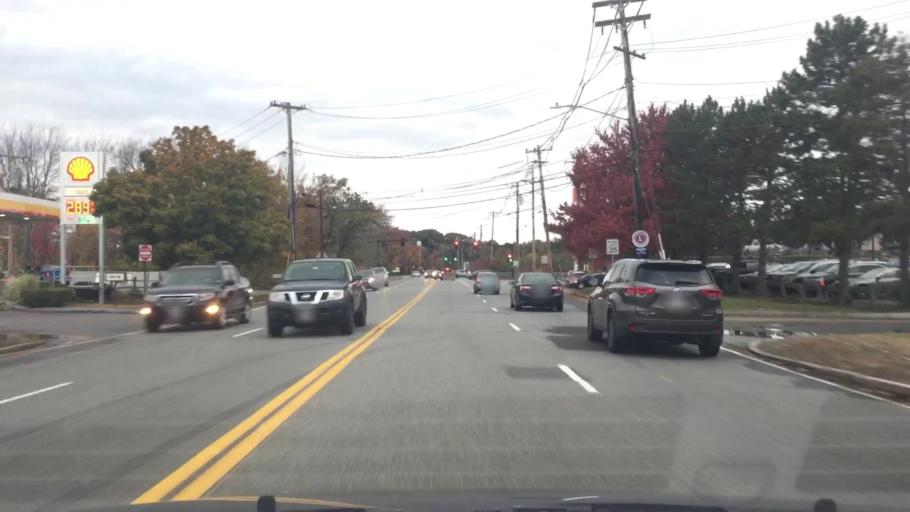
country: US
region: Massachusetts
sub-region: Middlesex County
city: Reading
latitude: 42.5160
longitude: -71.0887
